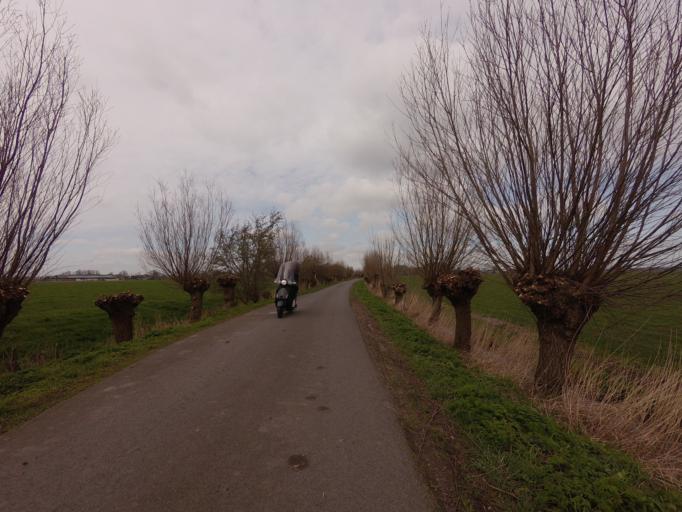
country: NL
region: North Holland
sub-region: Gemeente Amsterdam
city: Driemond
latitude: 52.2757
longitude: 5.0075
